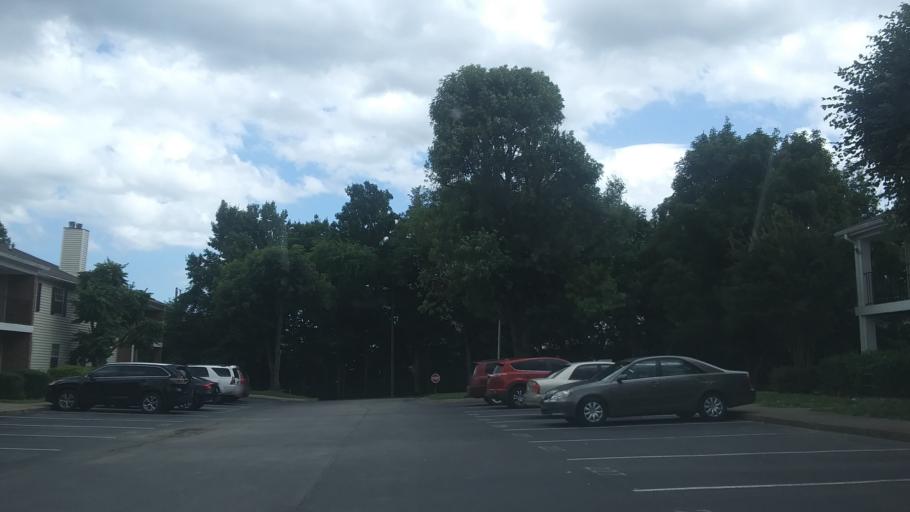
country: US
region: Tennessee
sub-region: Rutherford County
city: La Vergne
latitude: 36.0904
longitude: -86.6527
